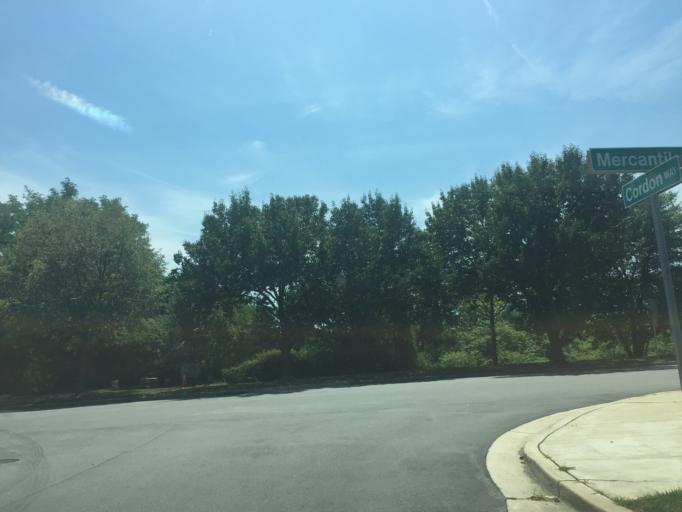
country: US
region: Maryland
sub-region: Baltimore County
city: White Marsh
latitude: 39.3770
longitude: -76.4588
